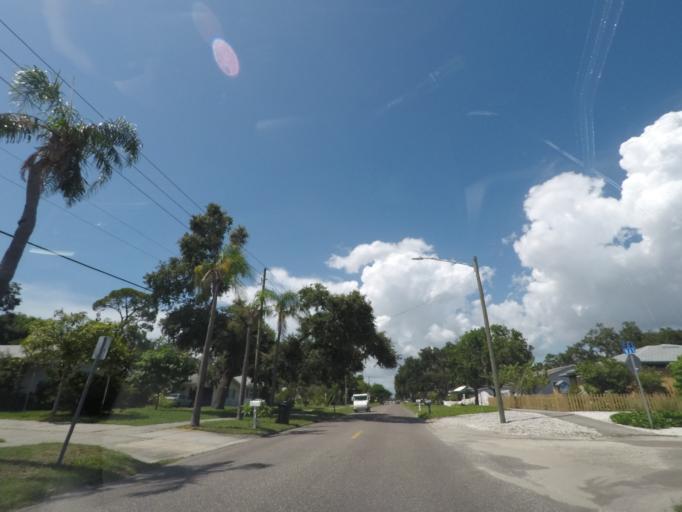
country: US
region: Florida
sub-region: Pinellas County
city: Gulfport
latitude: 27.7457
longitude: -82.7120
